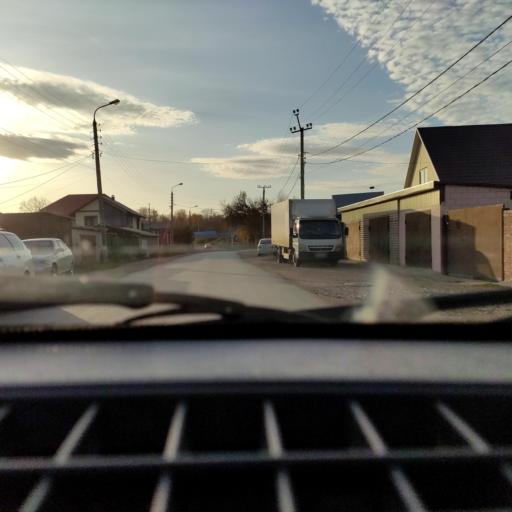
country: RU
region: Bashkortostan
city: Ufa
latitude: 54.6940
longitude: 55.9479
